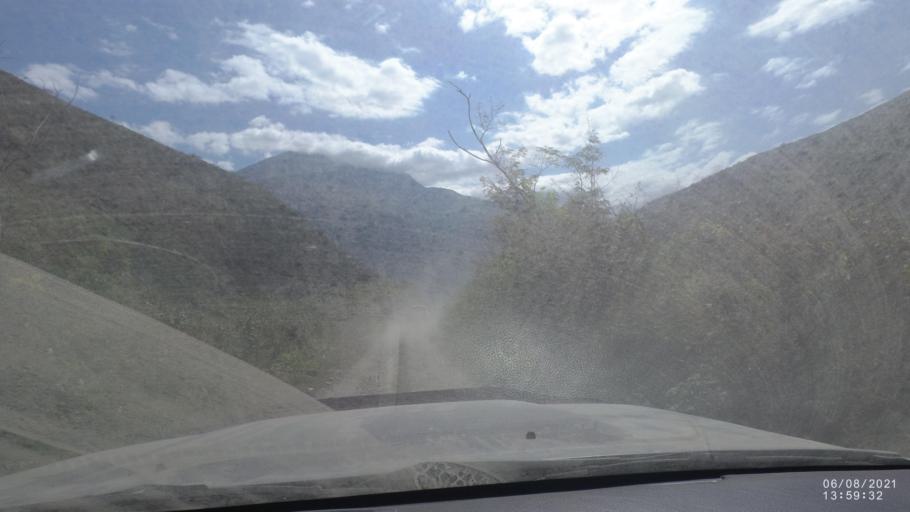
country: BO
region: La Paz
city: Quime
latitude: -16.6453
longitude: -66.7229
